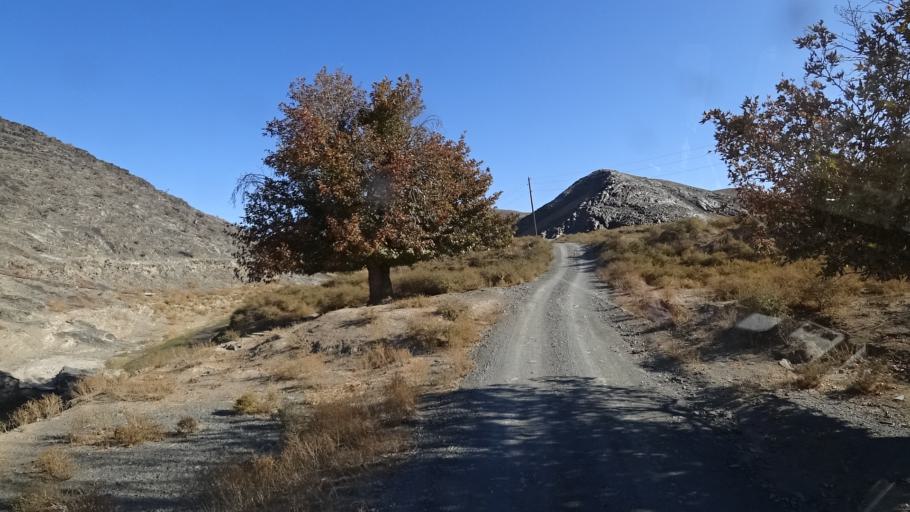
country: UZ
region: Navoiy
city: Nurota
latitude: 40.2993
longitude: 65.6116
